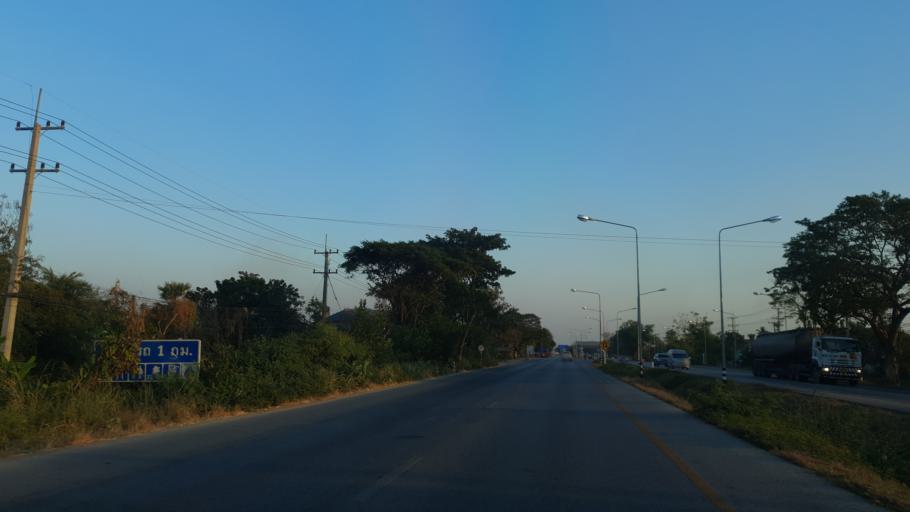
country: TH
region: Kamphaeng Phet
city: Khanu Woralaksaburi
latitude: 15.9759
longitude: 99.8283
